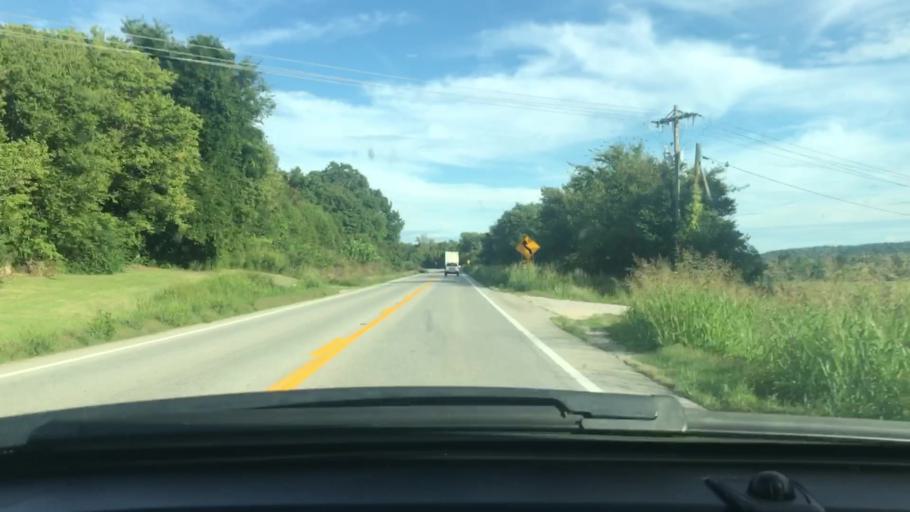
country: US
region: Arkansas
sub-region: Sharp County
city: Cherokee Village
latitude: 36.2989
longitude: -91.4392
